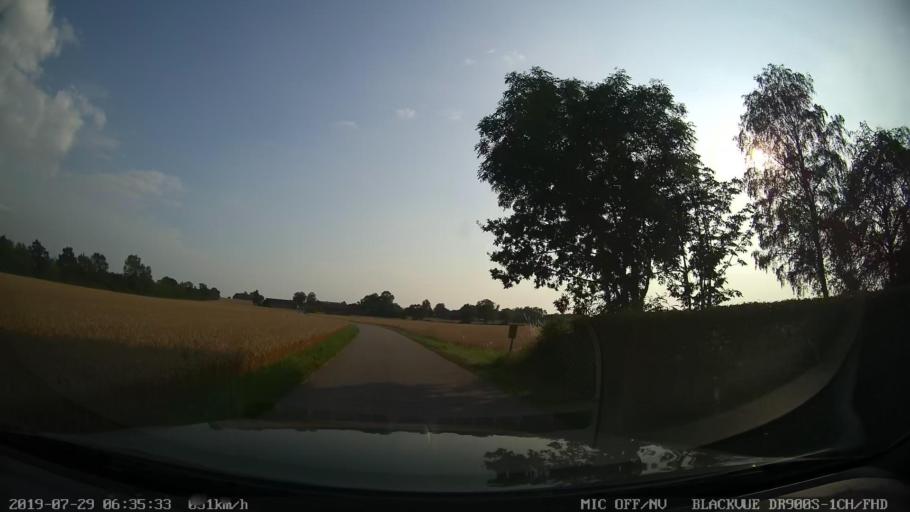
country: SE
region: Skane
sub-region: Helsingborg
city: Odakra
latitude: 56.1126
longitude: 12.7172
